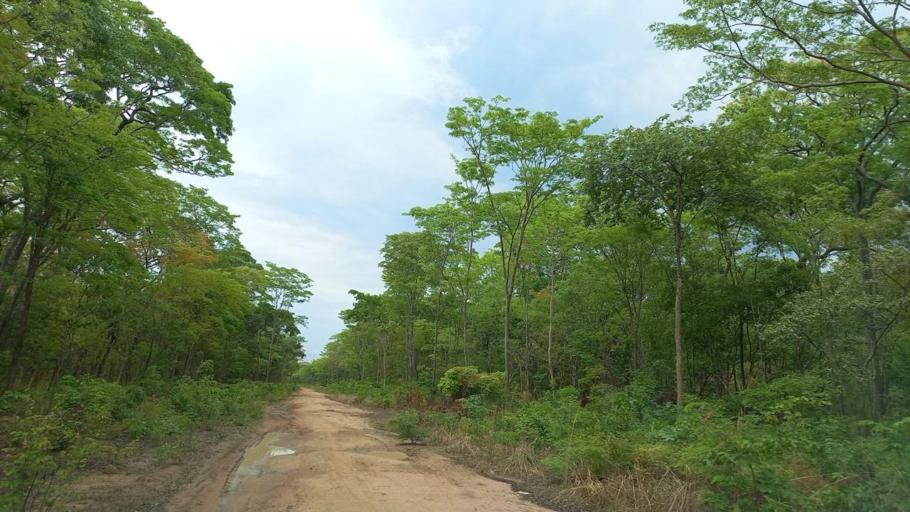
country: ZM
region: North-Western
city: Kalengwa
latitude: -13.5606
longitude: 24.9728
